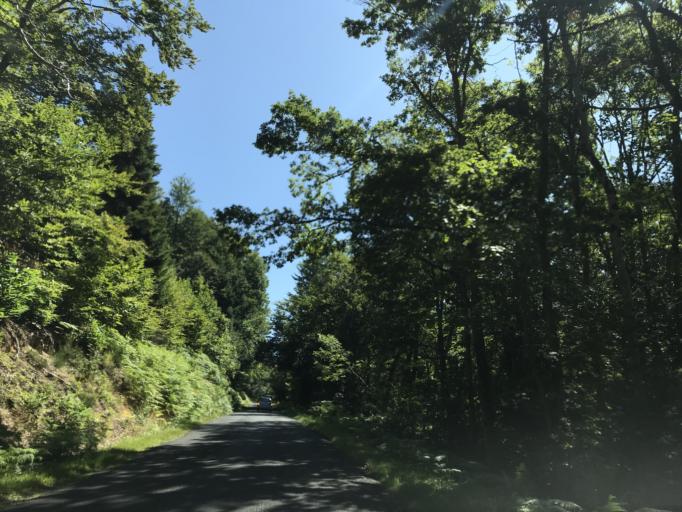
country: FR
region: Auvergne
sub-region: Departement du Puy-de-Dome
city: Job
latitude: 45.6698
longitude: 3.7352
